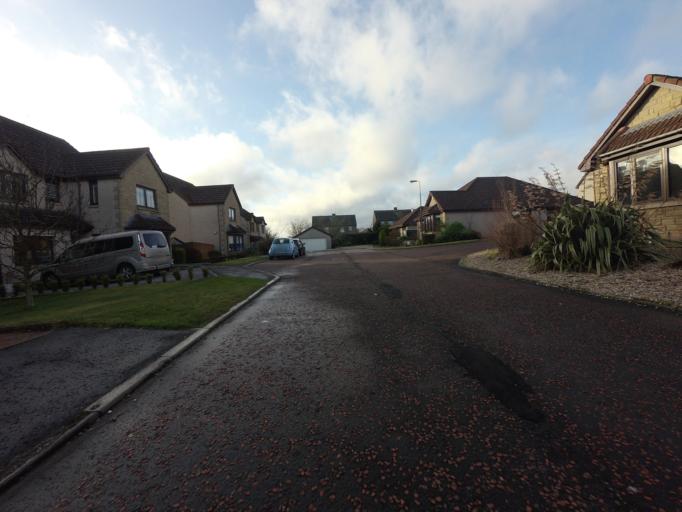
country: GB
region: Scotland
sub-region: West Lothian
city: West Calder
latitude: 55.8787
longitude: -3.5833
